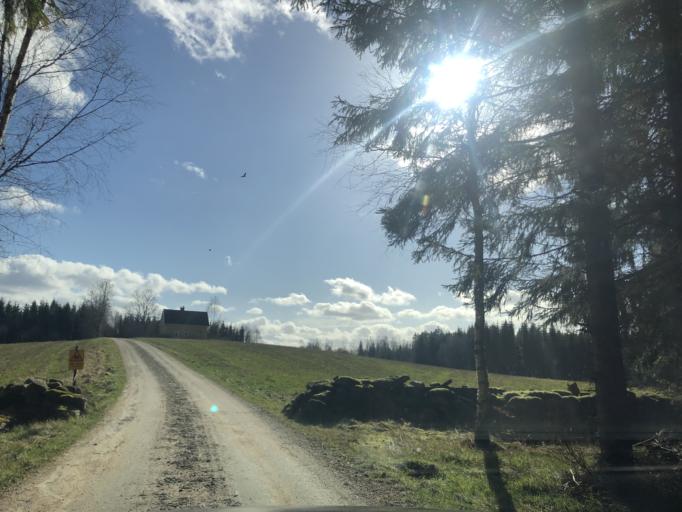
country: SE
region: Vaestra Goetaland
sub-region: Ulricehamns Kommun
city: Ulricehamn
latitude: 57.6873
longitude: 13.3773
